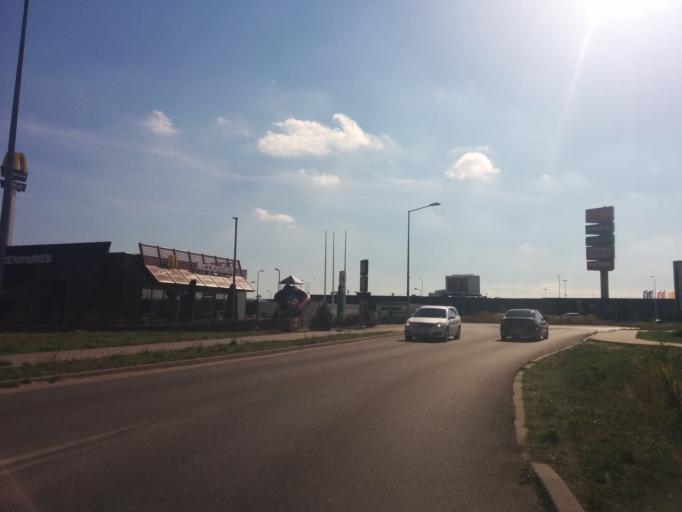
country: PL
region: Masovian Voivodeship
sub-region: Powiat wolominski
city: Marki
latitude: 52.3089
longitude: 21.0811
